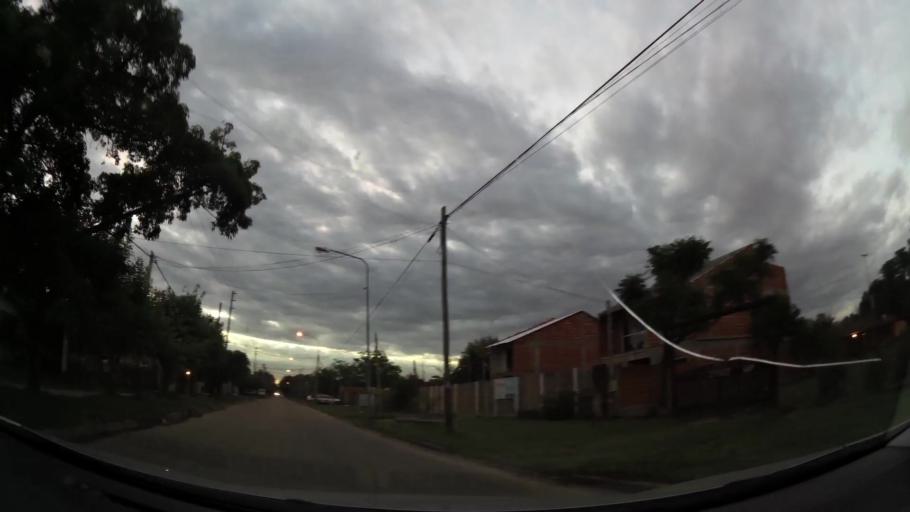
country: AR
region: Buenos Aires
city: Santa Catalina - Dique Lujan
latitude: -34.4165
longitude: -58.6815
